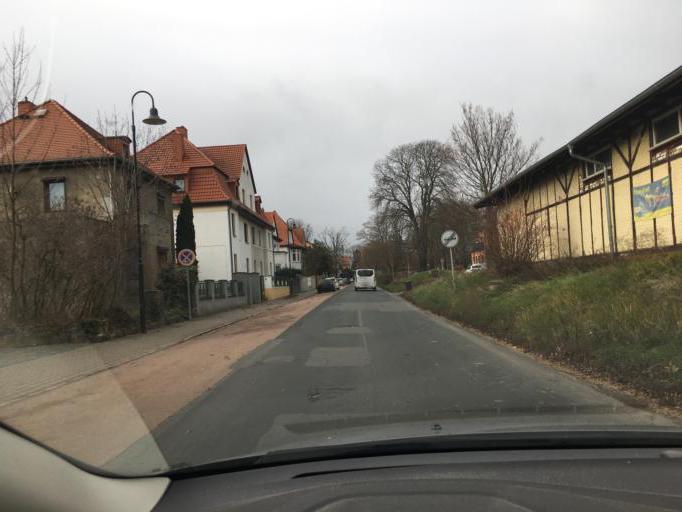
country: DE
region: Saxony-Anhalt
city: Bad Lauchstadt
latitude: 51.3885
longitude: 11.8737
